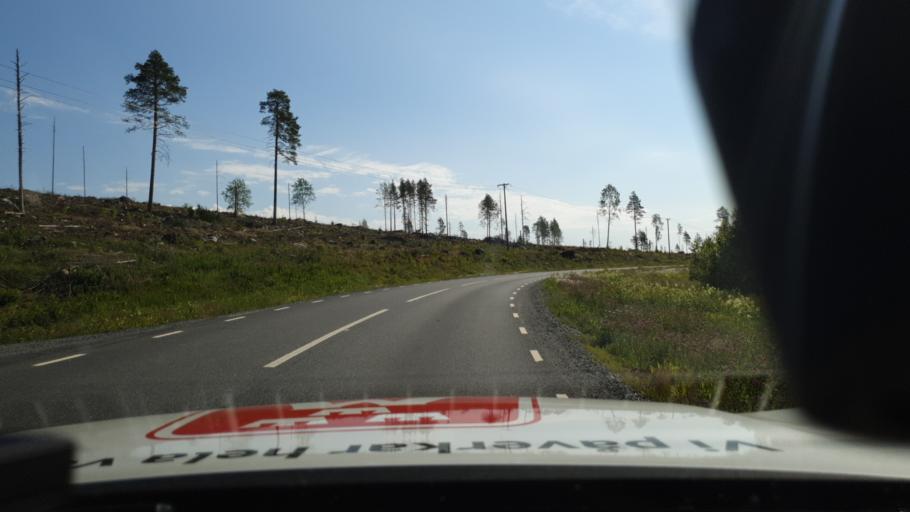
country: SE
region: Norrbotten
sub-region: Bodens Kommun
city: Saevast
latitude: 65.8360
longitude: 21.8538
